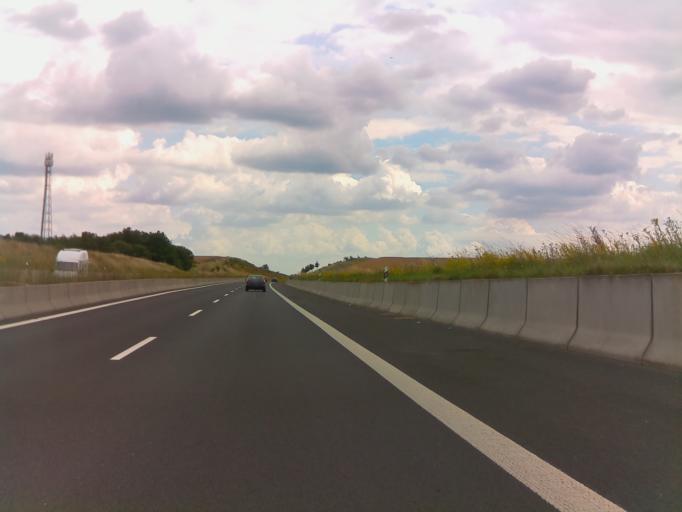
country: DE
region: Bavaria
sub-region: Regierungsbezirk Unterfranken
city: Munnerstadt
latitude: 50.2162
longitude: 10.2190
